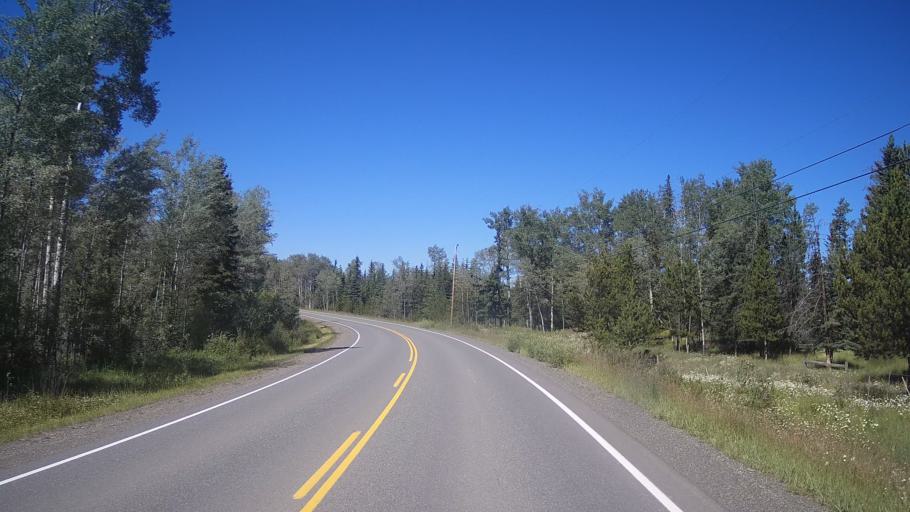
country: CA
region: British Columbia
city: Cache Creek
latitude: 51.5473
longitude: -120.9266
